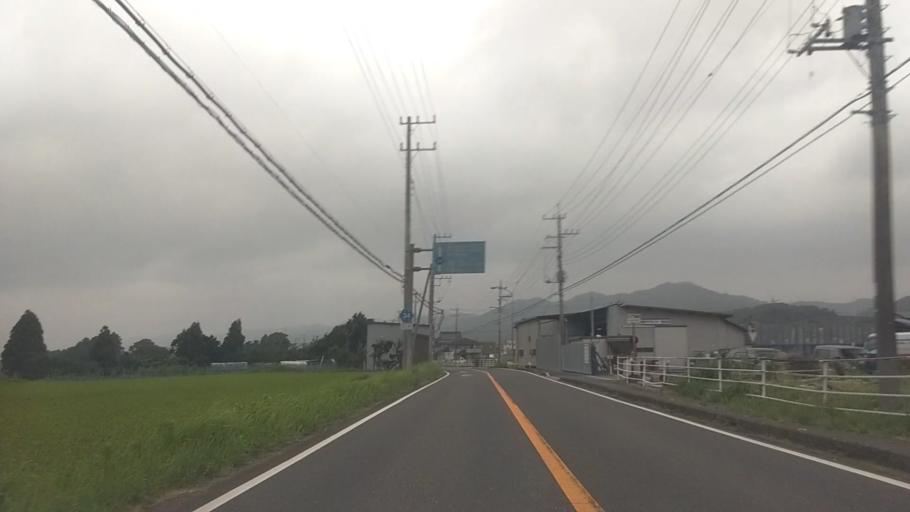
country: JP
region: Chiba
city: Kawaguchi
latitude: 35.1243
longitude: 140.0601
